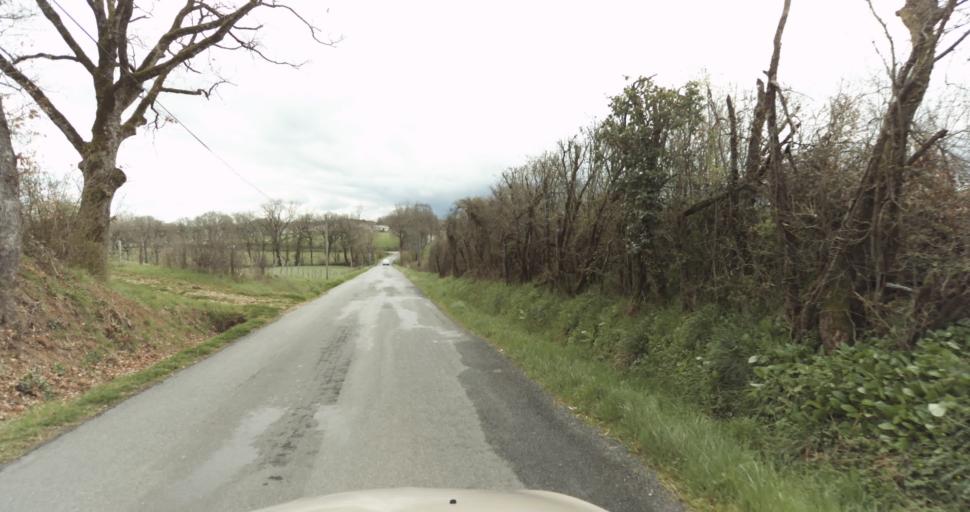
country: FR
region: Midi-Pyrenees
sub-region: Departement du Tarn
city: Puygouzon
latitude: 43.8875
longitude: 2.1949
